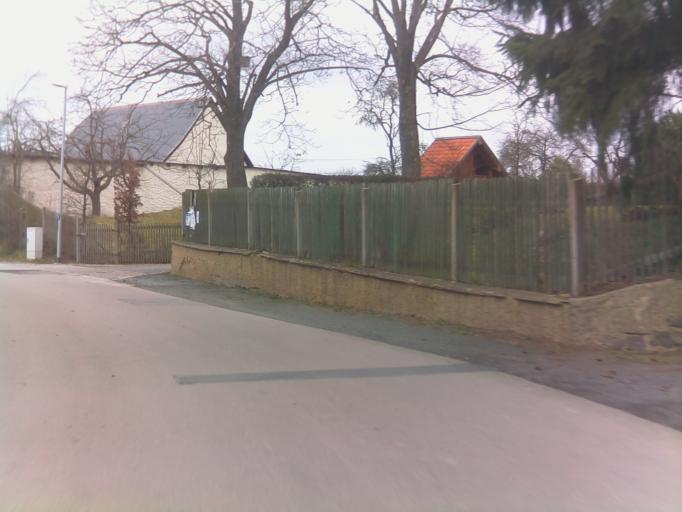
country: DE
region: Thuringia
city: Auma
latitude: 50.6786
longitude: 11.9290
